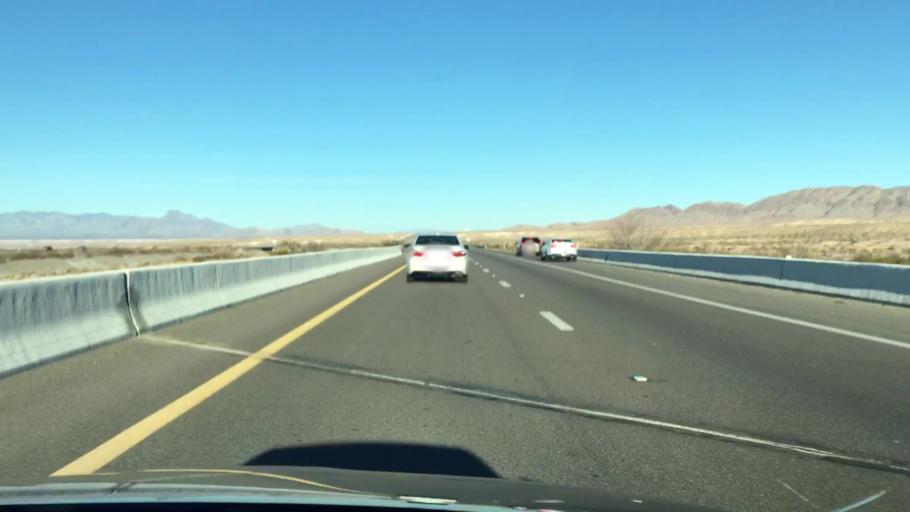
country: US
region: Nevada
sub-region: Clark County
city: Moapa Town
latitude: 36.5551
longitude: -114.6917
